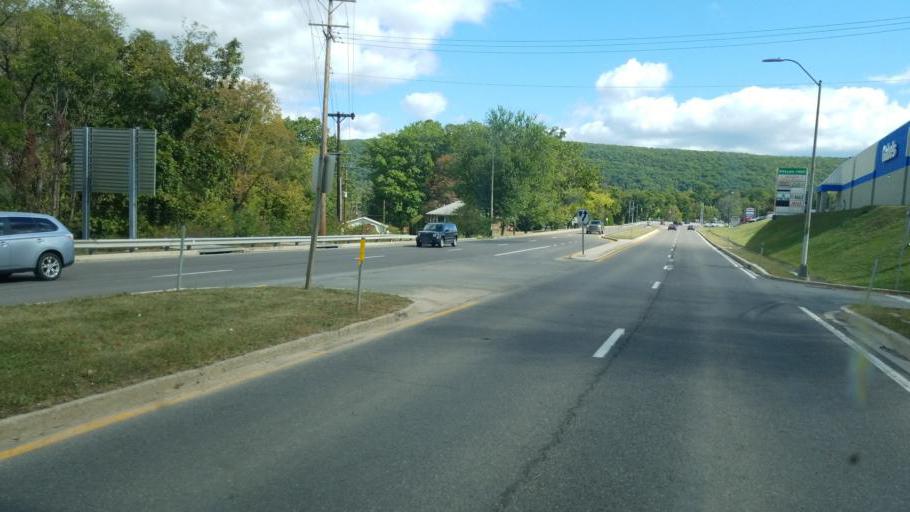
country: US
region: Maryland
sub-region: Allegany County
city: La Vale
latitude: 39.6342
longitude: -78.8420
